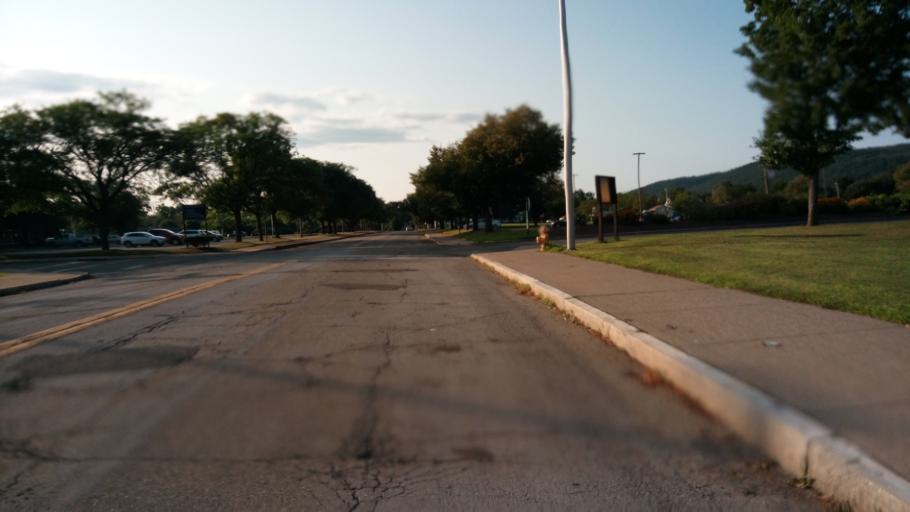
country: US
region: New York
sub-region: Chemung County
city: Elmira
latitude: 42.0914
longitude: -76.7954
